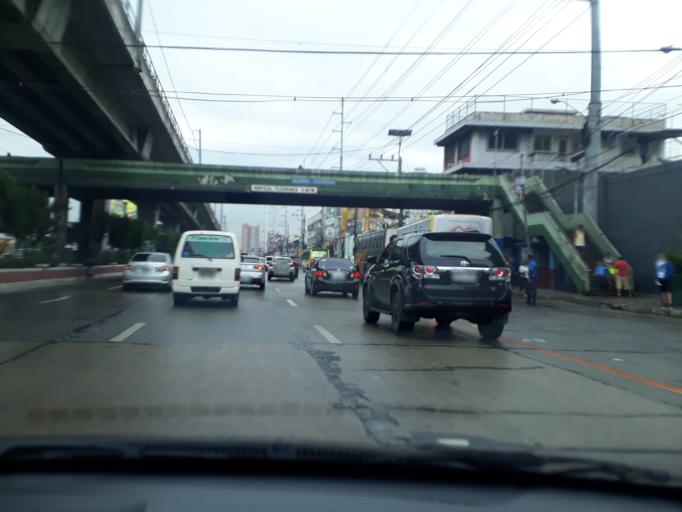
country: PH
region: Calabarzon
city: Del Monte
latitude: 14.6574
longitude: 121.0064
